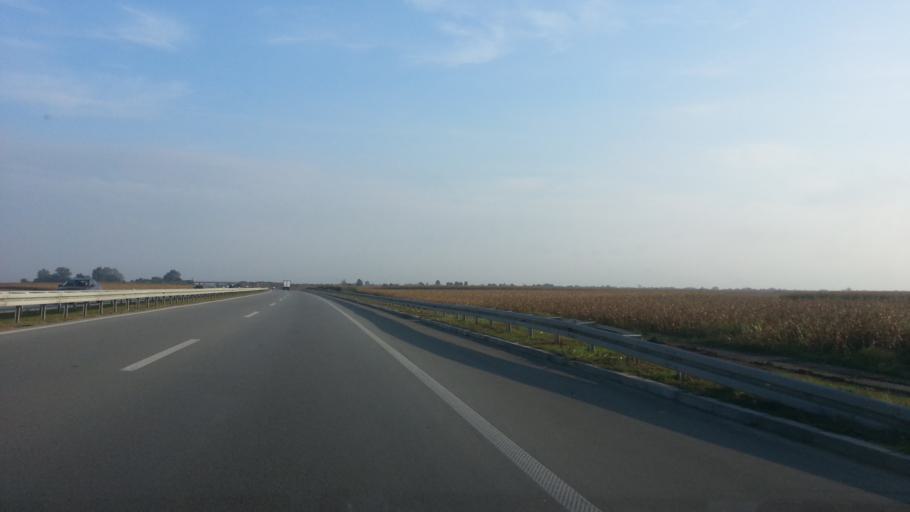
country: RS
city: Novi Banovci
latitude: 44.9078
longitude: 20.3051
